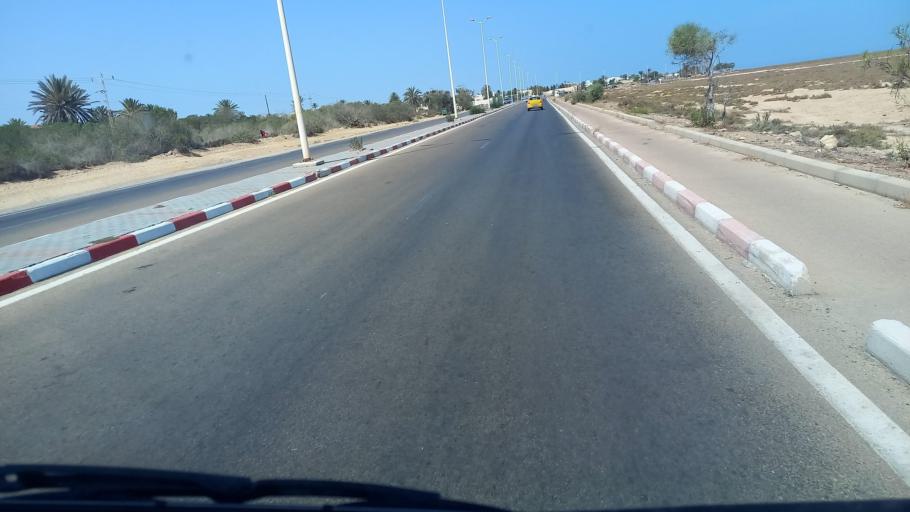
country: TN
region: Madanin
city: Midoun
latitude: 33.8691
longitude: 10.9417
